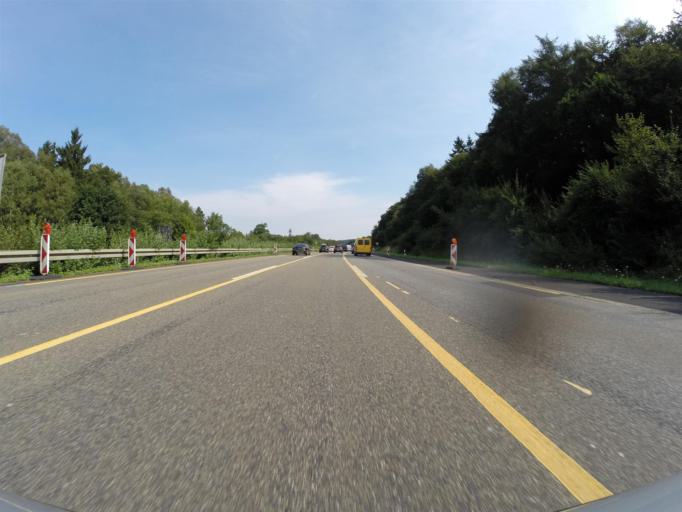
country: DE
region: Hesse
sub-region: Regierungsbezirk Kassel
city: Korle
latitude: 51.1184
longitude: 9.4846
